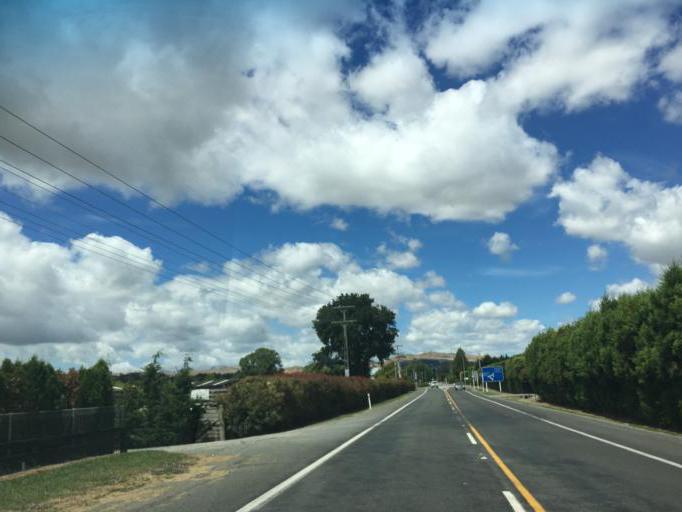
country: NZ
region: Hawke's Bay
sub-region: Hastings District
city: Hastings
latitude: -39.6567
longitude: 176.8869
